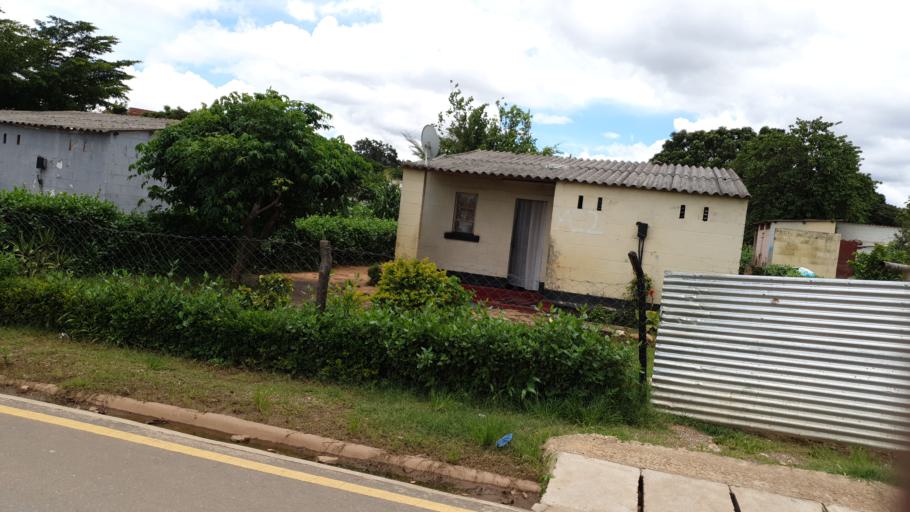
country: ZM
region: Lusaka
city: Lusaka
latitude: -15.4259
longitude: 28.3052
